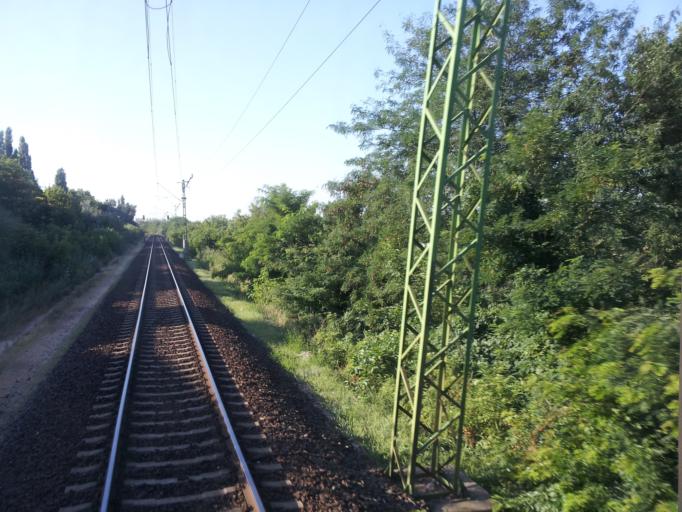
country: HU
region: Budapest
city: Budapest XX. keruelet
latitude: 47.4219
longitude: 19.1050
